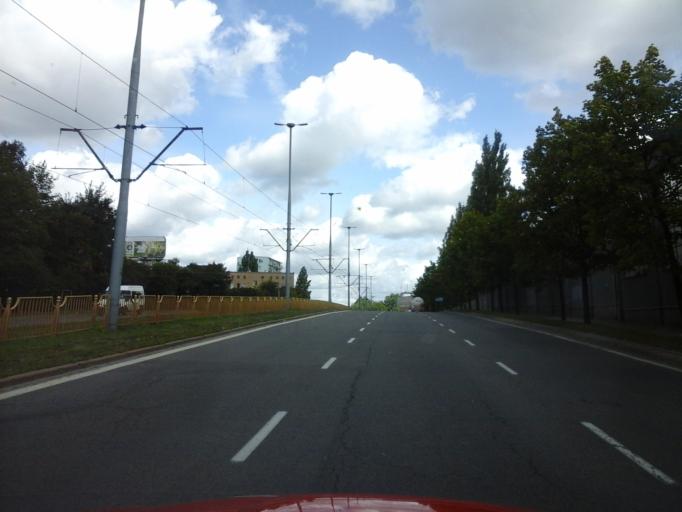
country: PL
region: West Pomeranian Voivodeship
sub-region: Szczecin
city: Szczecin
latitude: 53.4352
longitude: 14.5733
